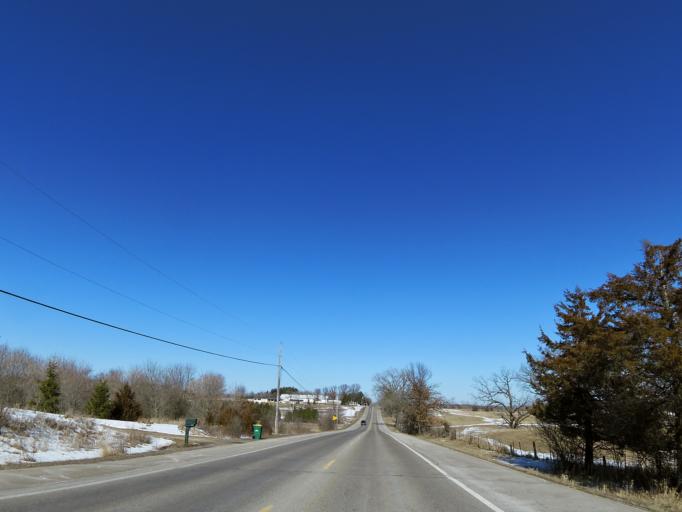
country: US
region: Minnesota
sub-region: Washington County
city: Grant
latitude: 45.0523
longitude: -92.8835
